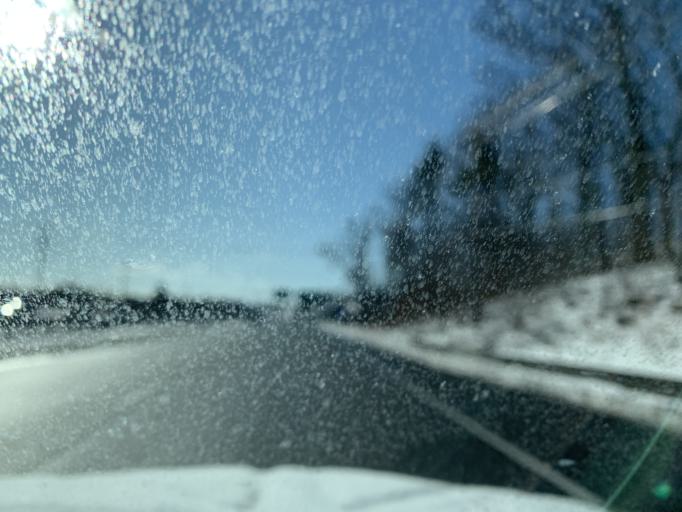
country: US
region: Massachusetts
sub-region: Essex County
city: Danvers
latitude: 42.5874
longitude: -70.9659
